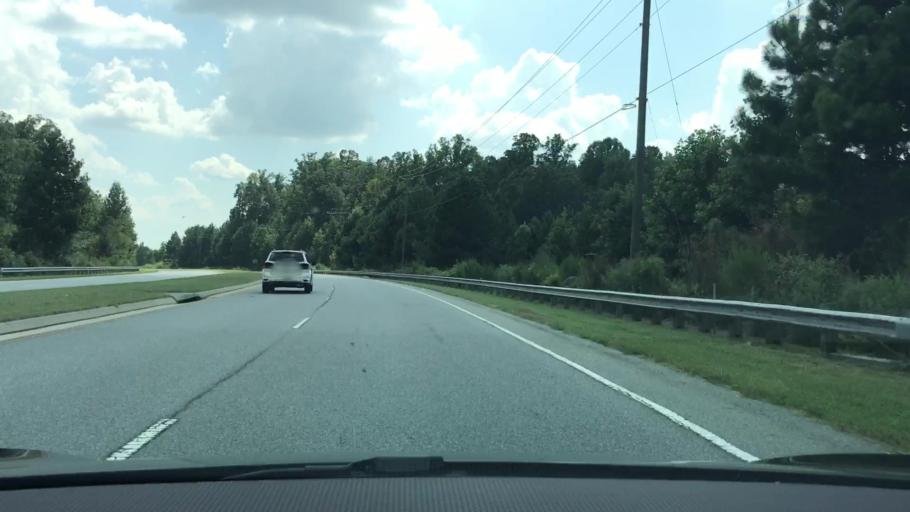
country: US
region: Georgia
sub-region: Gwinnett County
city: Sugar Hill
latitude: 34.0739
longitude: -84.0181
